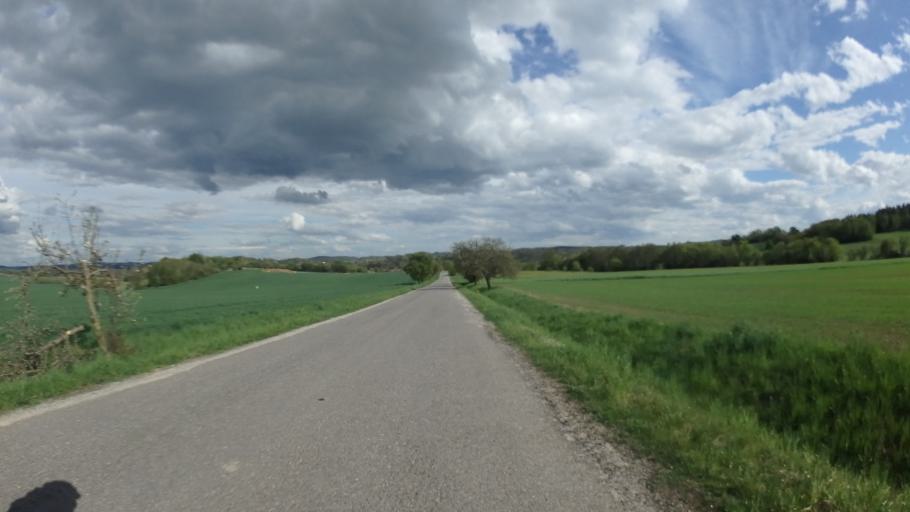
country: CZ
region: Vysocina
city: Merin
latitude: 49.3423
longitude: 15.8904
